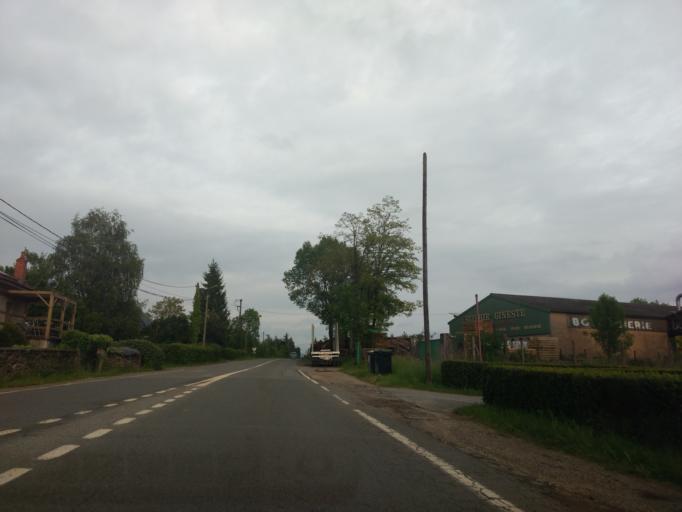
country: FR
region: Midi-Pyrenees
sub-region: Departement de l'Aveyron
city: Montbazens
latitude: 44.4608
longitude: 2.2230
